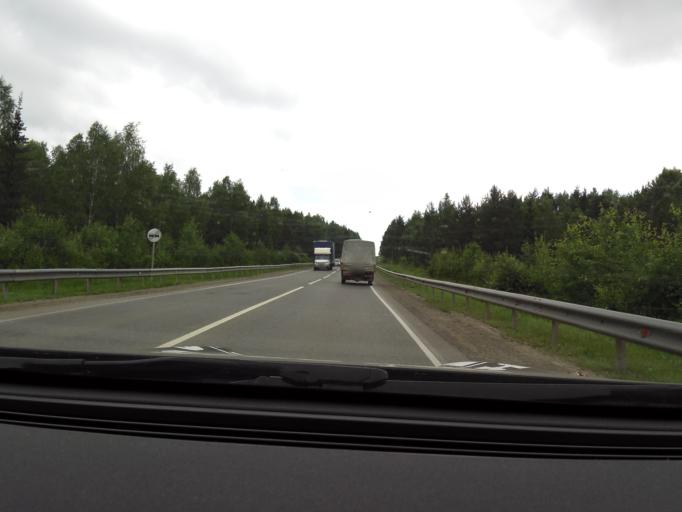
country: RU
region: Perm
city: Kukushtan
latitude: 57.5886
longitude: 56.5476
